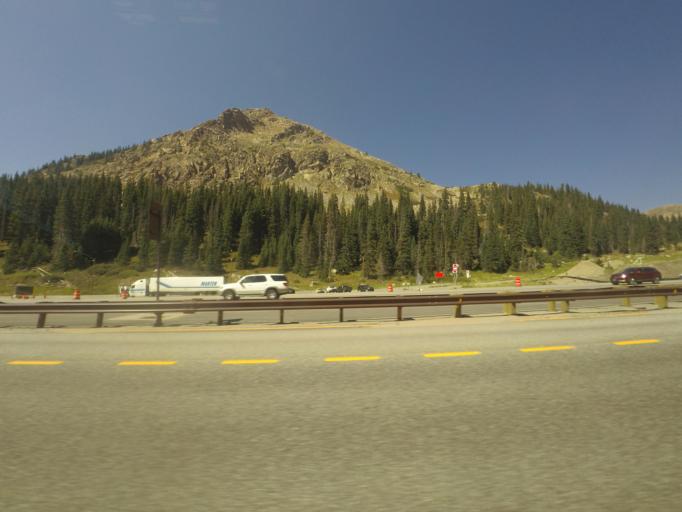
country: US
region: Colorado
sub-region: Summit County
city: Keystone
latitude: 39.6759
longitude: -105.9358
